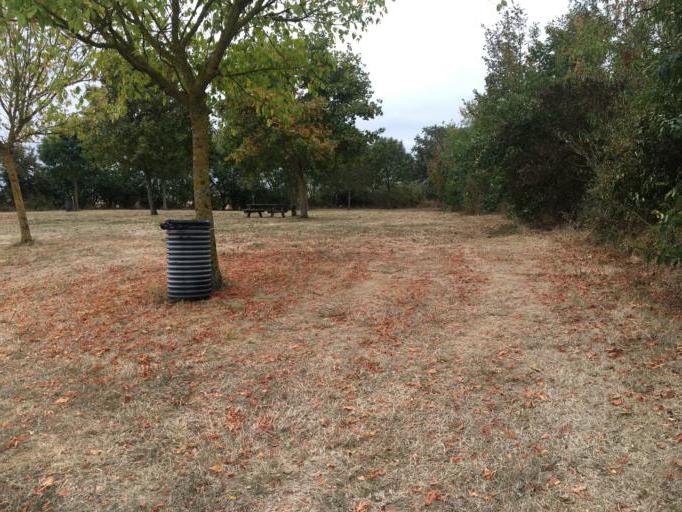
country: FR
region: Poitou-Charentes
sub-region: Departement des Deux-Sevres
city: Beauvoir-sur-Niort
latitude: 46.0865
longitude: -0.5004
